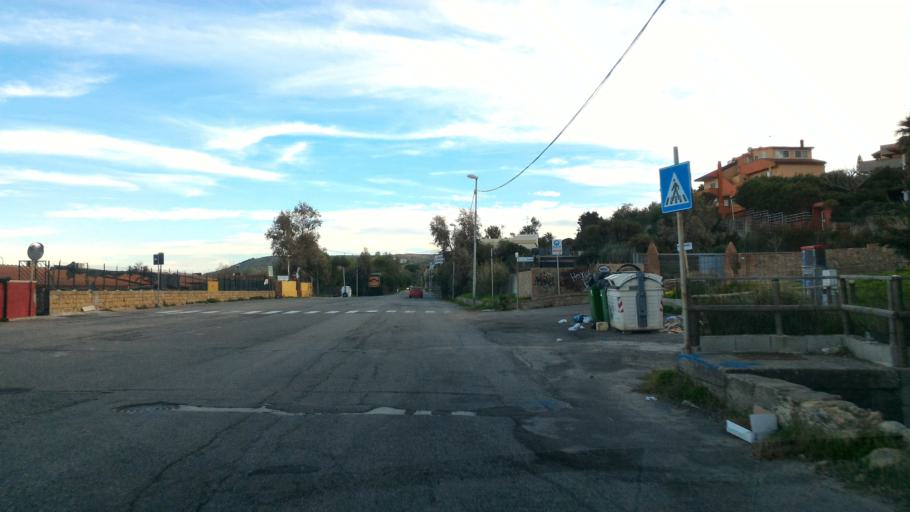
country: IT
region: Calabria
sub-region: Provincia di Crotone
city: Crotone
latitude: 39.0568
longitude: 17.1355
